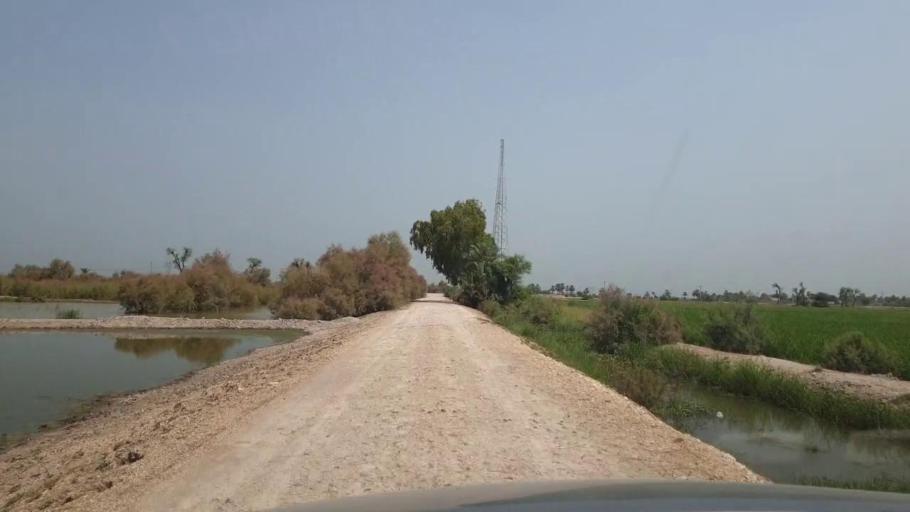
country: PK
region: Sindh
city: Madeji
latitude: 27.8021
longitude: 68.5318
